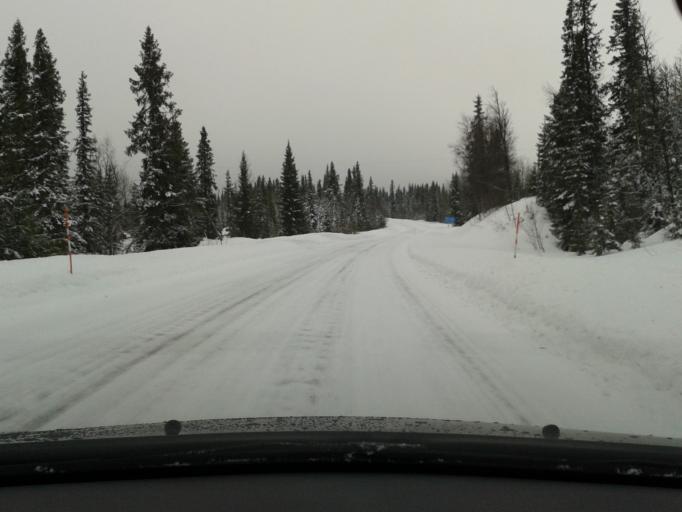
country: SE
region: Vaesterbotten
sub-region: Vilhelmina Kommun
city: Sjoberg
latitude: 65.1436
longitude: 15.8710
